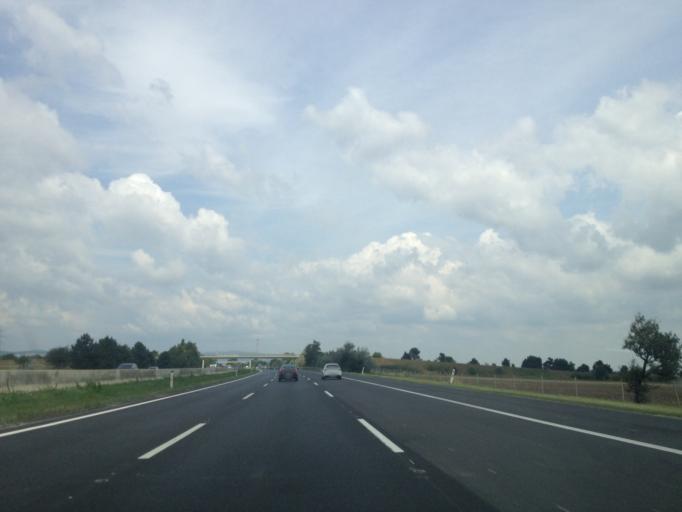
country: AT
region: Lower Austria
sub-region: Politischer Bezirk Wiener Neustadt
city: Felixdorf
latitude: 47.8830
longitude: 16.2040
